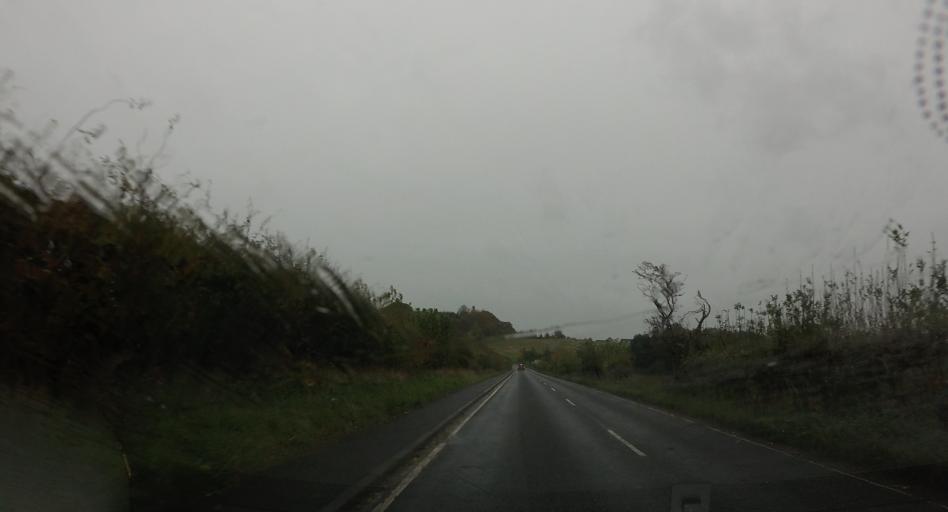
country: GB
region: Scotland
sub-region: Perth and Kinross
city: Coupar Angus
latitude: 56.5498
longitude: -3.2822
